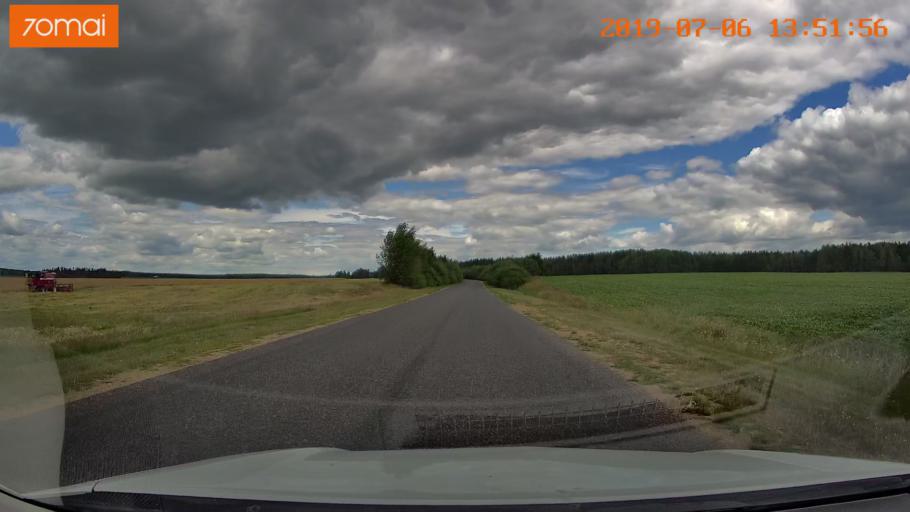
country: BY
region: Minsk
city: Ivyanyets
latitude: 53.7142
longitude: 26.8295
